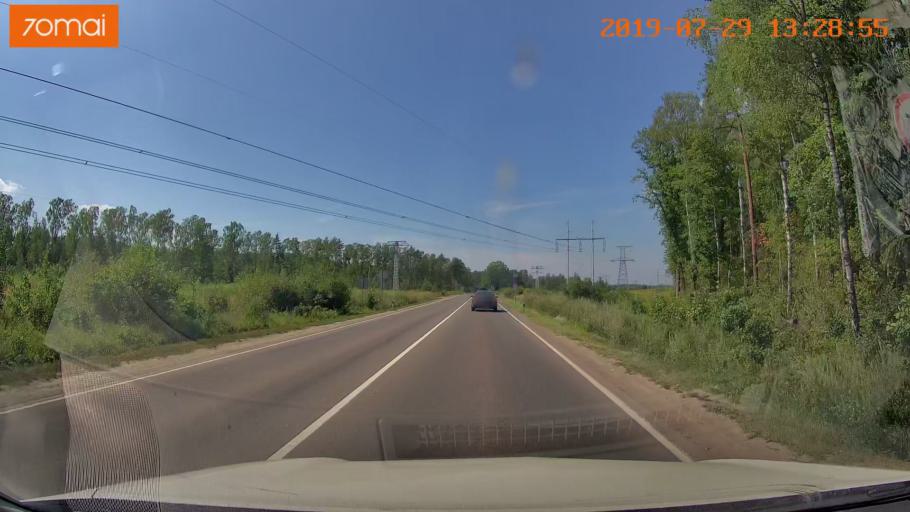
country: RU
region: Kaliningrad
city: Vzmorye
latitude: 54.7038
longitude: 20.2760
